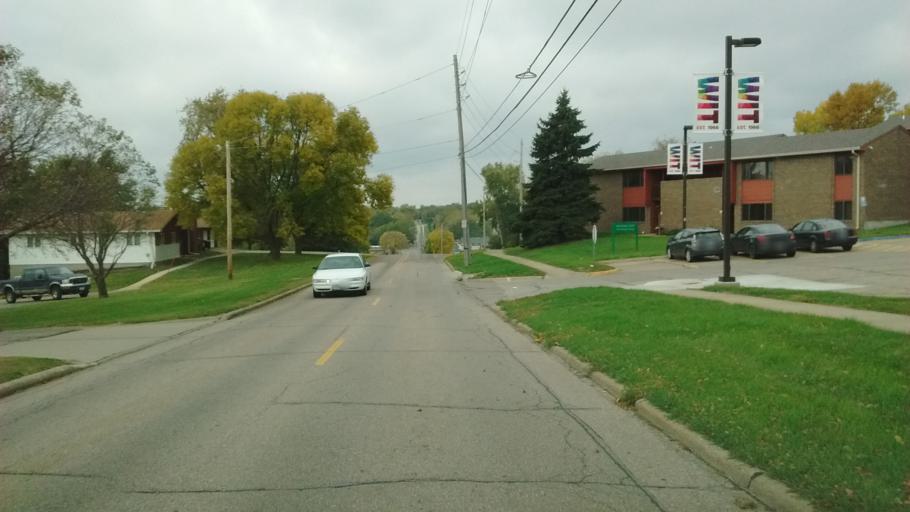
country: US
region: Iowa
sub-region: Woodbury County
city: Sioux City
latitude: 42.4792
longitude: -96.3449
